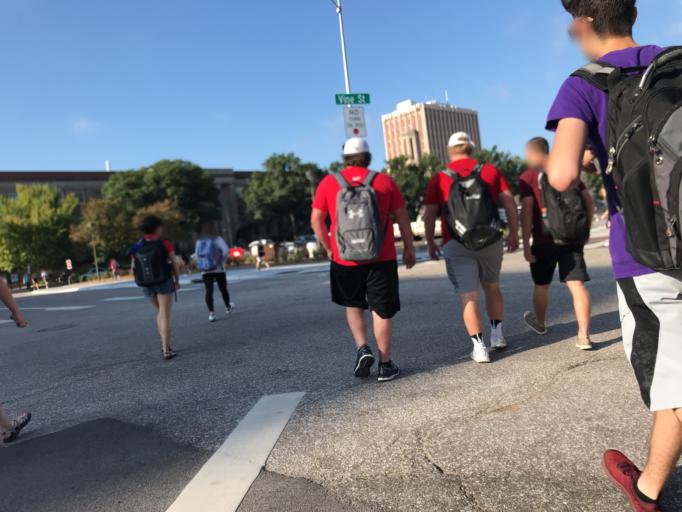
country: US
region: Nebraska
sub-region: Lancaster County
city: Lincoln
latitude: 40.8210
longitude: -96.7012
